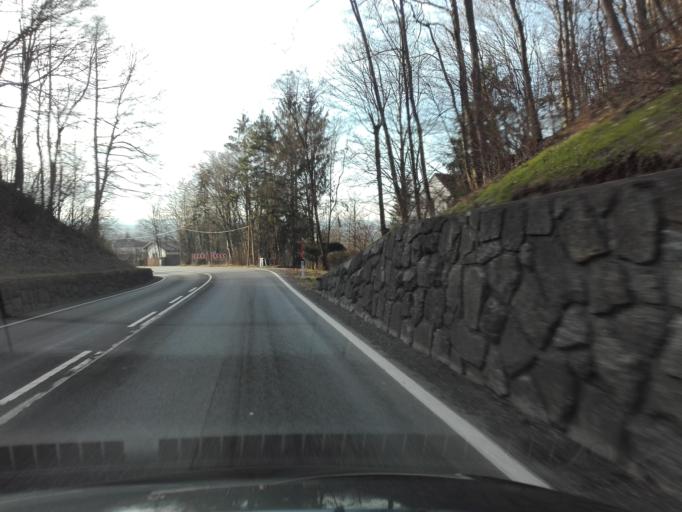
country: AT
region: Lower Austria
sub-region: Politischer Bezirk Amstetten
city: Sankt Valentin
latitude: 48.1883
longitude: 14.5530
